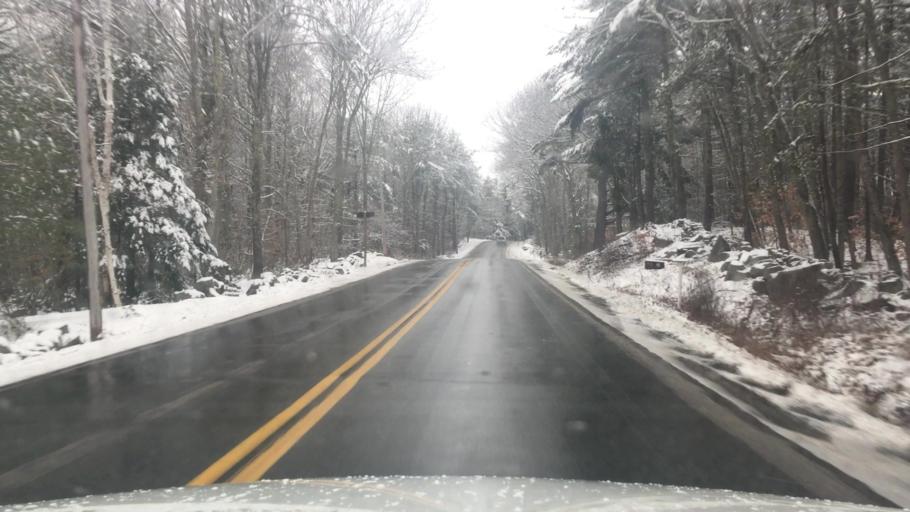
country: US
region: Maine
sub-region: Lincoln County
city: Jefferson
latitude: 44.2059
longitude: -69.4794
